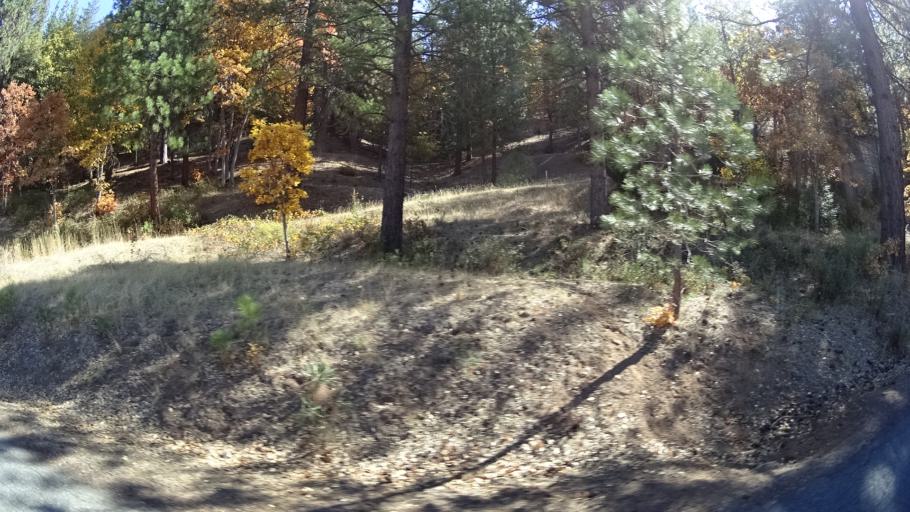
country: US
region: California
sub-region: Siskiyou County
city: Yreka
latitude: 41.5839
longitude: -122.9574
